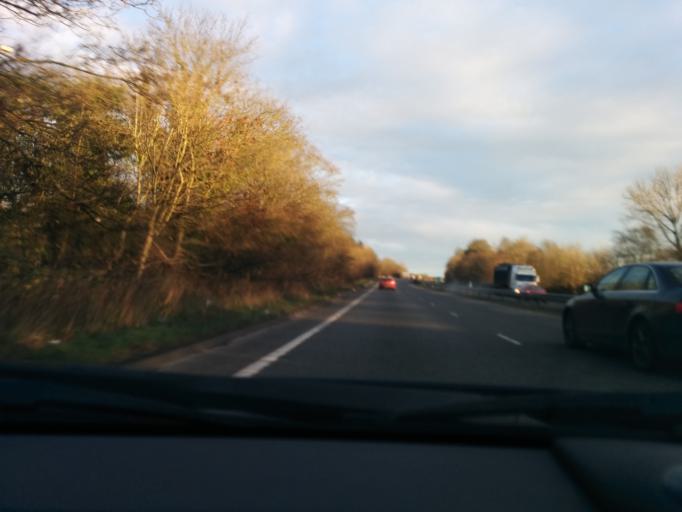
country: GB
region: England
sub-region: Oxfordshire
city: Wheatley
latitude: 51.7480
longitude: -1.1282
